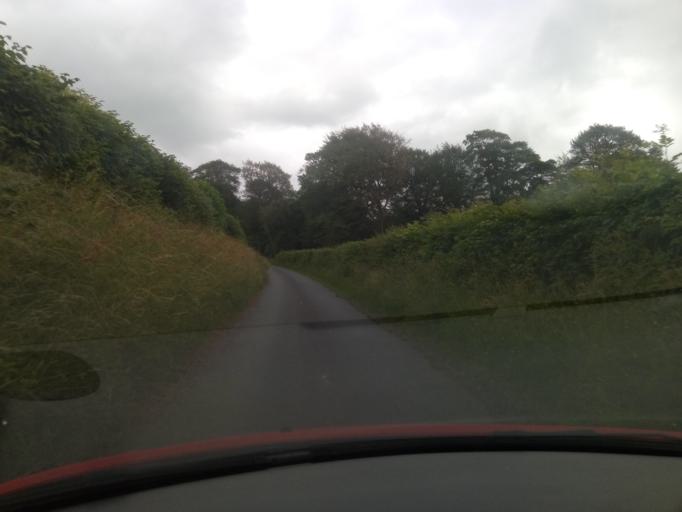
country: GB
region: Scotland
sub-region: The Scottish Borders
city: Hawick
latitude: 55.4189
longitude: -2.8159
